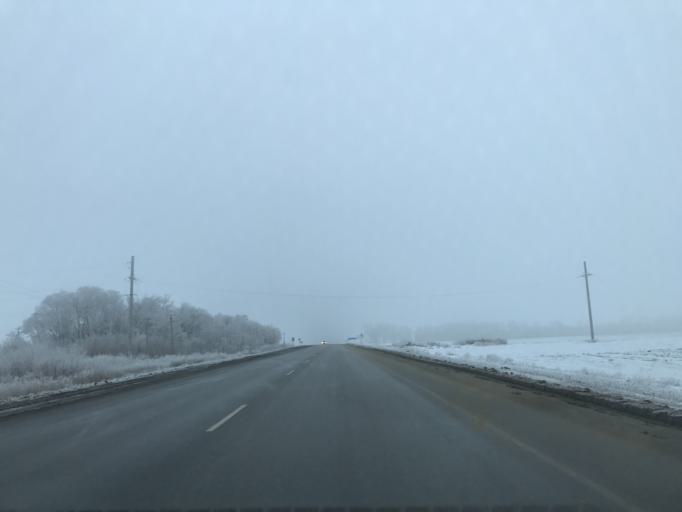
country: RU
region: Rostov
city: Temernik
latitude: 47.3782
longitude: 39.8273
